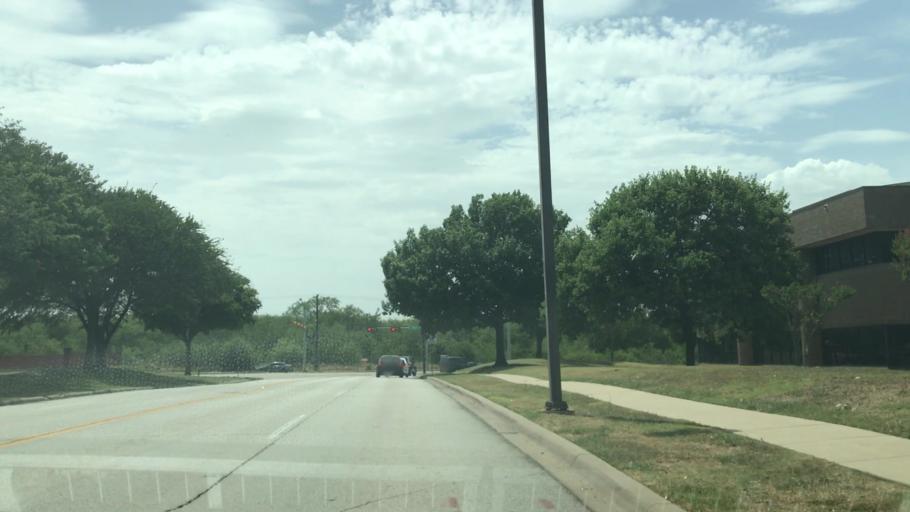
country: US
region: Texas
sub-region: Dallas County
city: Coppell
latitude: 32.8940
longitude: -96.9899
